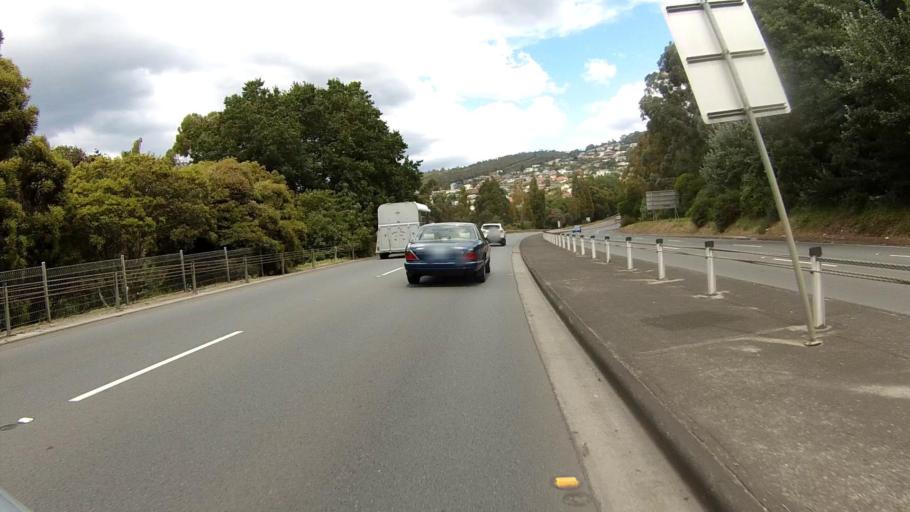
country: AU
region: Tasmania
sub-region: Hobart
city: Sandy Bay
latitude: -42.8942
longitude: 147.3183
